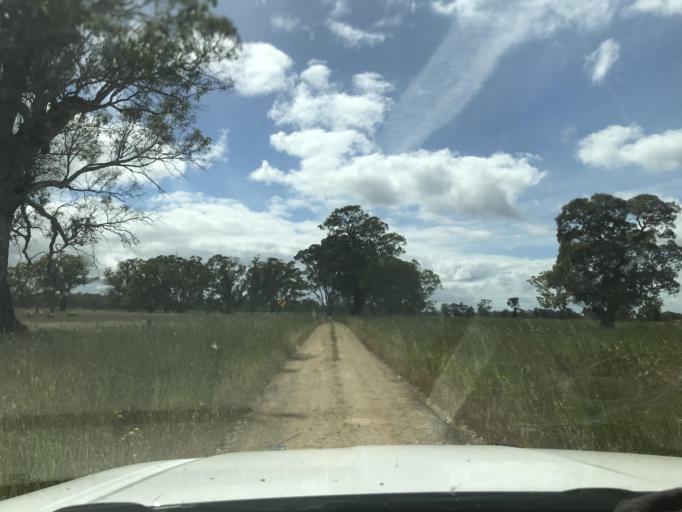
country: AU
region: South Australia
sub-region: Naracoorte and Lucindale
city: Naracoorte
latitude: -37.0109
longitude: 141.0878
